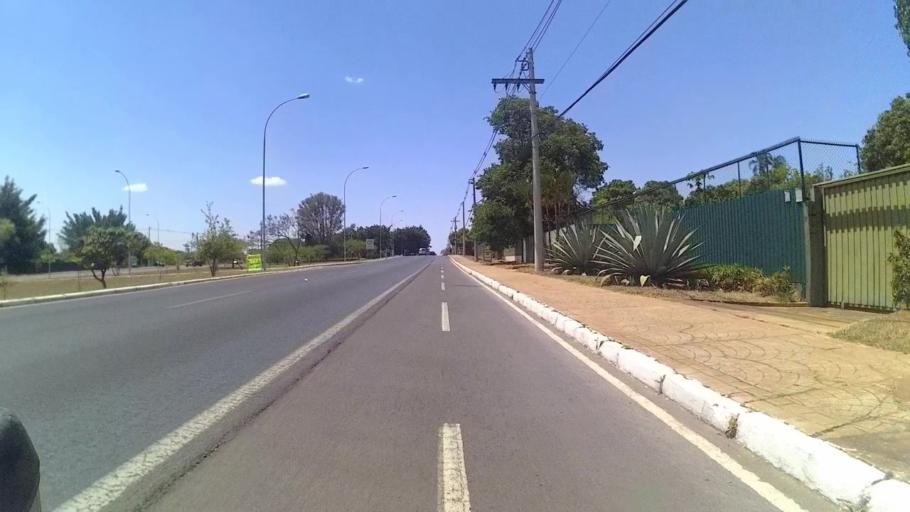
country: BR
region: Federal District
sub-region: Brasilia
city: Brasilia
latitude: -15.7314
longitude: -47.8675
